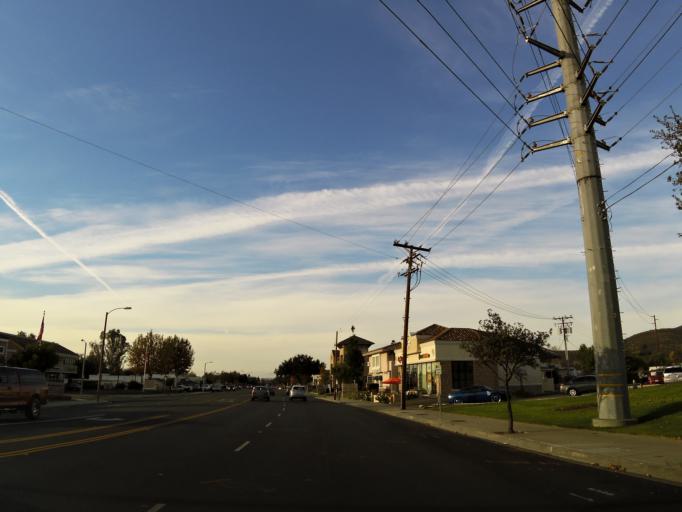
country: US
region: California
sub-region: Ventura County
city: Thousand Oaks
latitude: 34.1670
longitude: -118.8332
